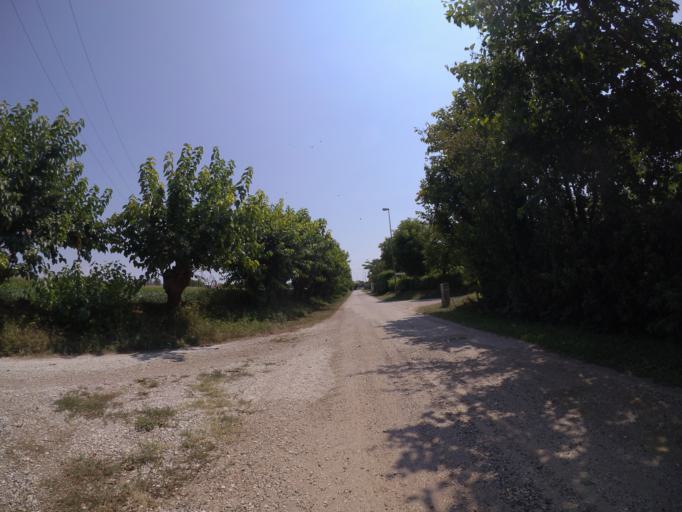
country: IT
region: Friuli Venezia Giulia
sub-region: Provincia di Udine
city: Castions di Strada
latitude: 45.9173
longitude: 13.1781
